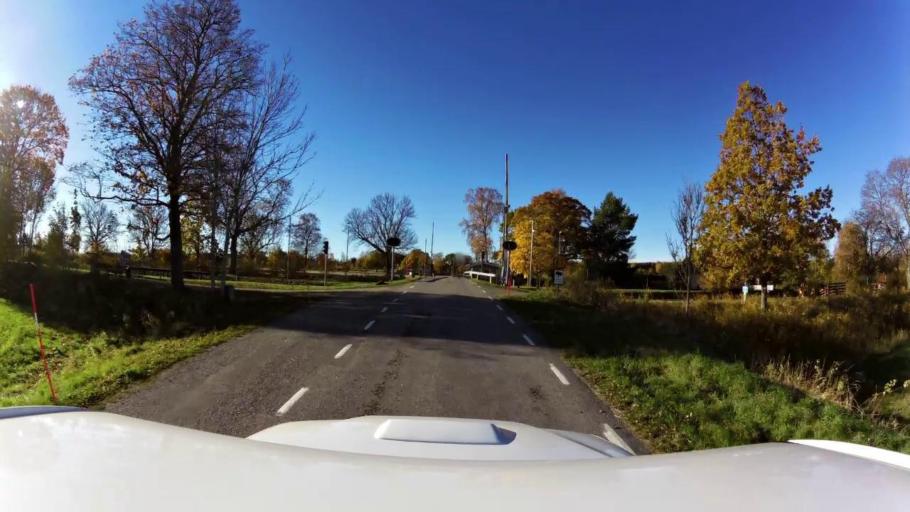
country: SE
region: OEstergoetland
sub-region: Linkopings Kommun
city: Ljungsbro
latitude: 58.5334
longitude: 15.3929
